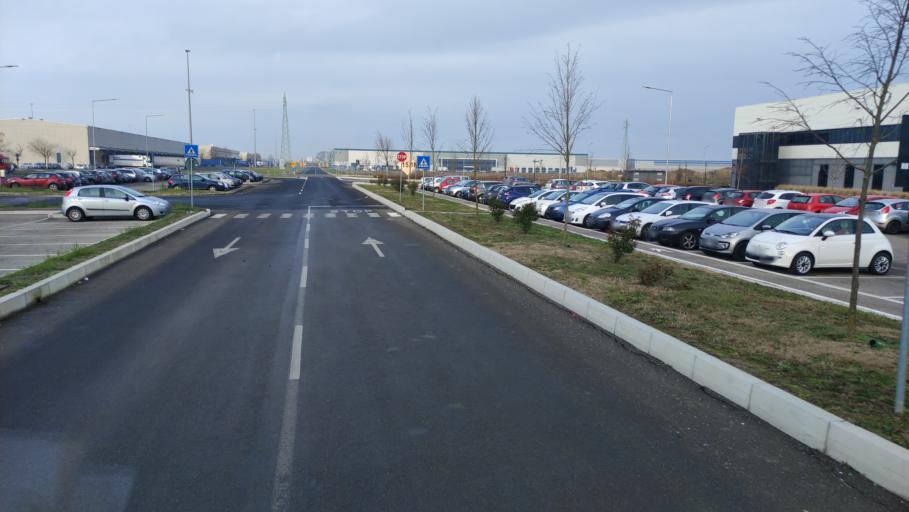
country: IT
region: Emilia-Romagna
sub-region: Provincia di Bologna
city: San Giorgio di Piano
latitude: 44.6296
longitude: 11.3927
